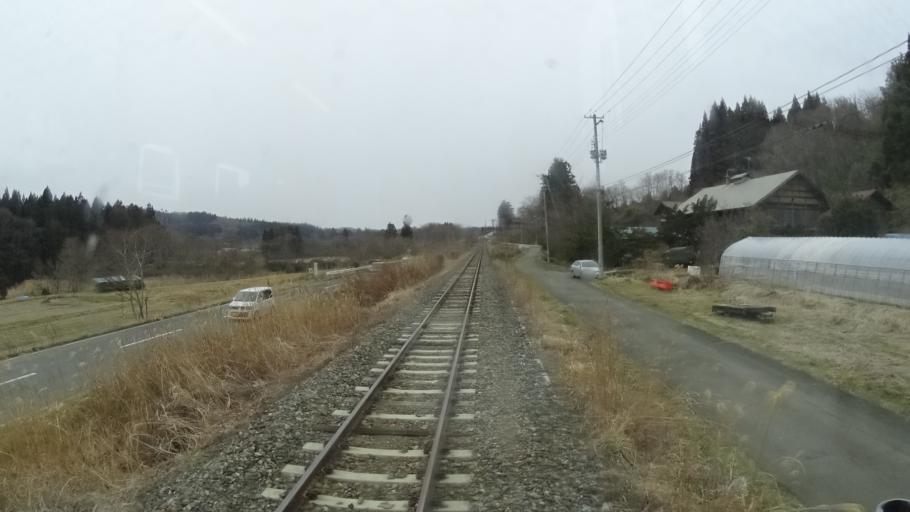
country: JP
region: Iwate
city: Hanamaki
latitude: 39.3620
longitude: 141.2738
